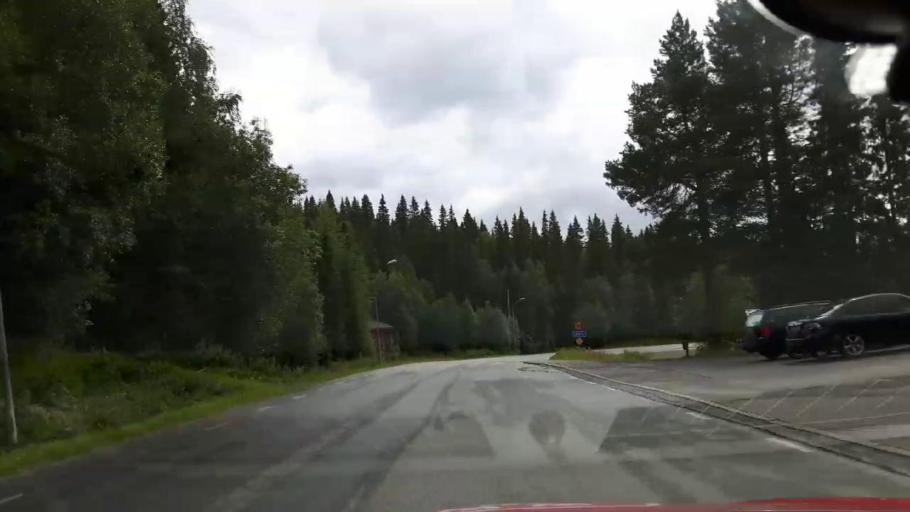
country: NO
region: Nord-Trondelag
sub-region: Lierne
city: Sandvika
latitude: 64.4962
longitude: 14.1494
